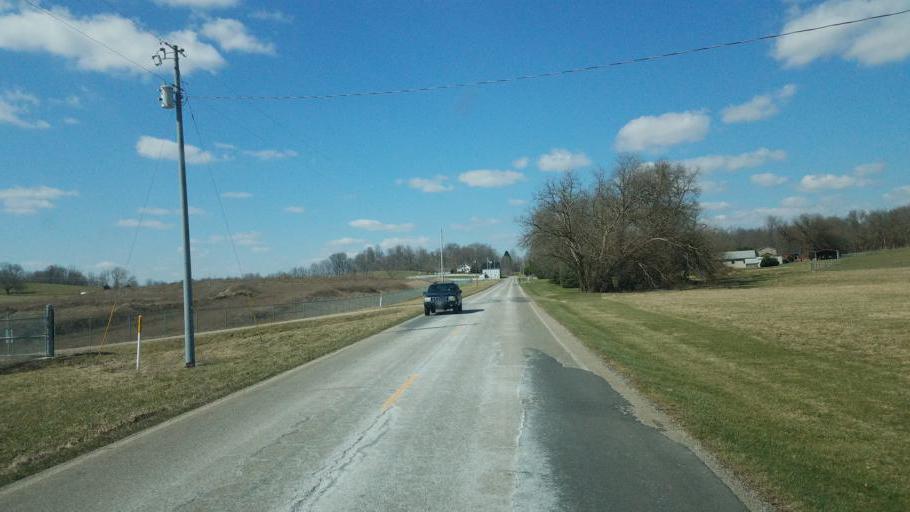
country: US
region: Ohio
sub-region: Knox County
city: Fredericktown
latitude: 40.4561
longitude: -82.5176
